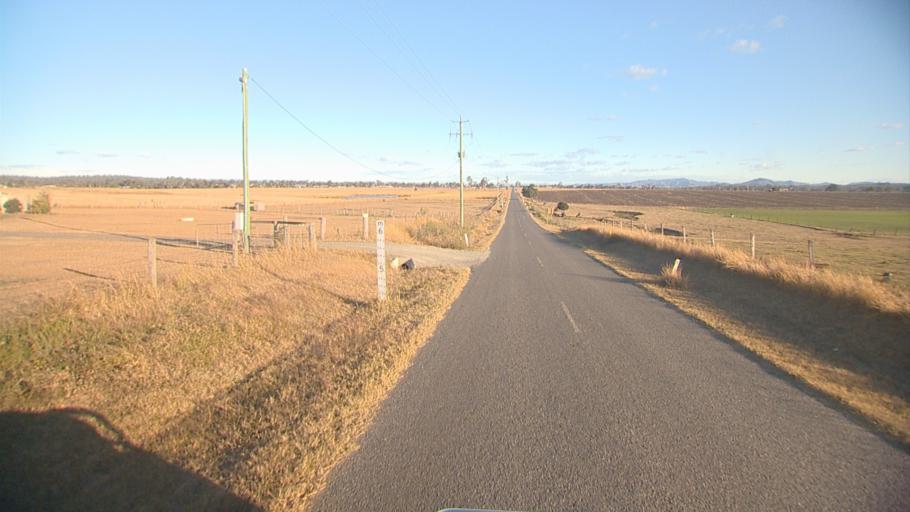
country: AU
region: Queensland
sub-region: Logan
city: Cedar Vale
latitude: -27.8597
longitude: 152.9592
